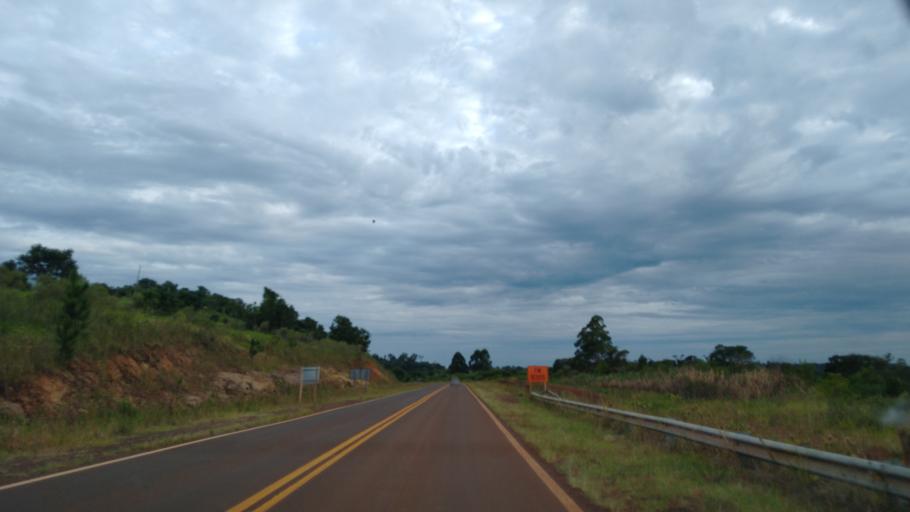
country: AR
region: Misiones
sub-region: Departamento de San Pedro
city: San Pedro
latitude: -26.5330
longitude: -53.9402
